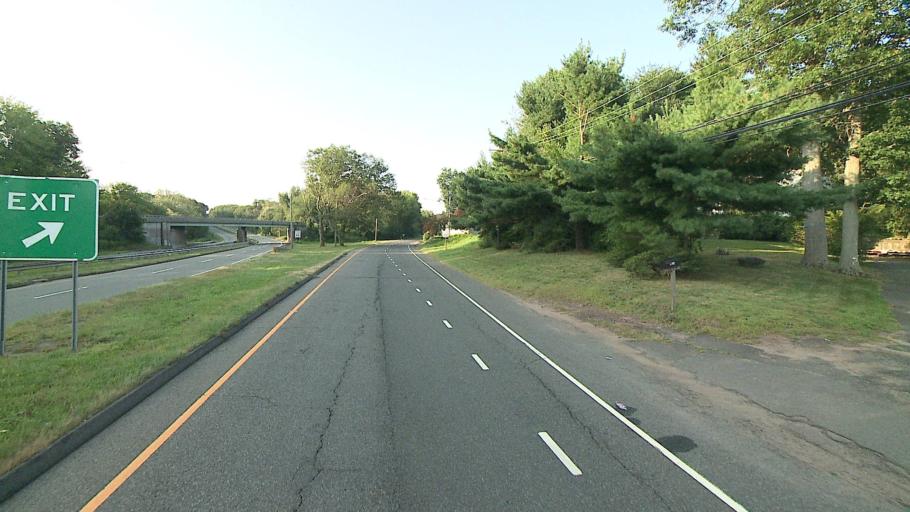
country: US
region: Connecticut
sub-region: New Haven County
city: Meriden
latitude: 41.5601
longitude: -72.7762
